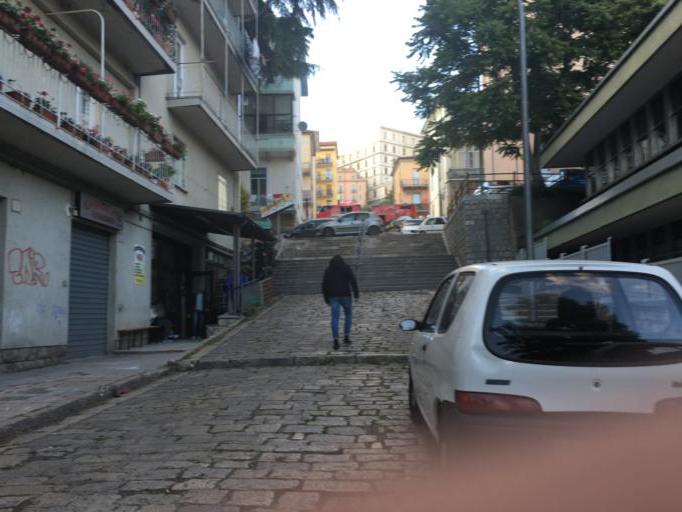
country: IT
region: Basilicate
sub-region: Provincia di Potenza
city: Potenza
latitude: 40.6360
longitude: 15.8055
